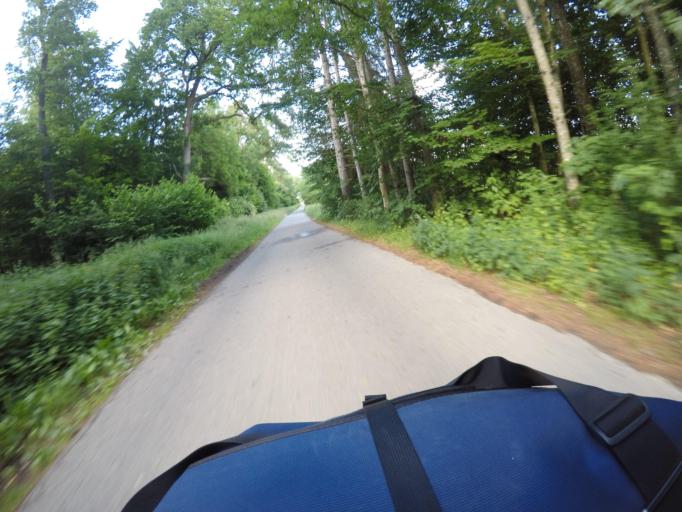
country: DE
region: Baden-Wuerttemberg
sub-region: Regierungsbezirk Stuttgart
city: Nufringen
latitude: 48.6283
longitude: 8.8693
